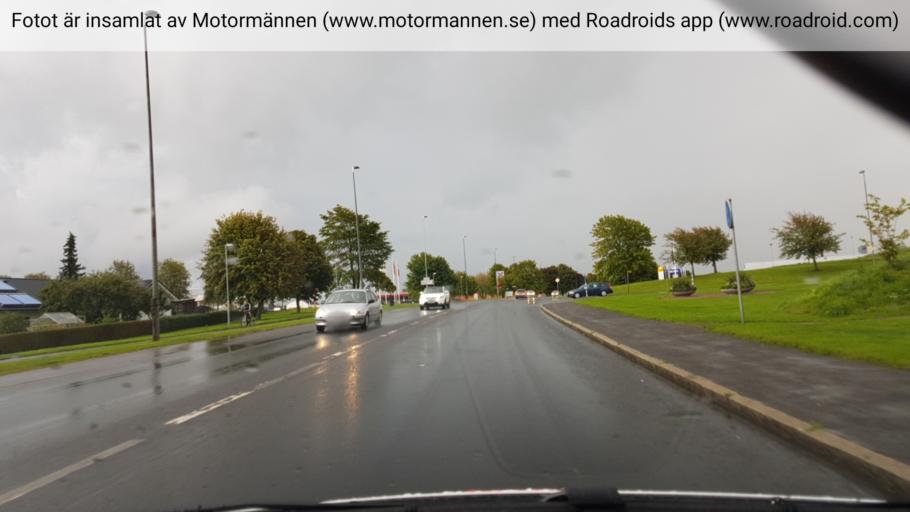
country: SE
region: Vaestra Goetaland
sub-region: Falkopings Kommun
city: Falkoeping
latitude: 58.1705
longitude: 13.5765
